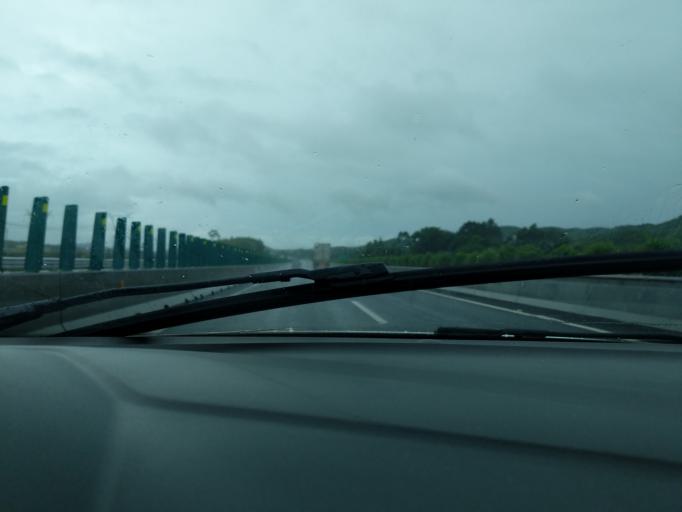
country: CN
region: Guangdong
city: Liangxi
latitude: 22.2655
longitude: 112.3213
